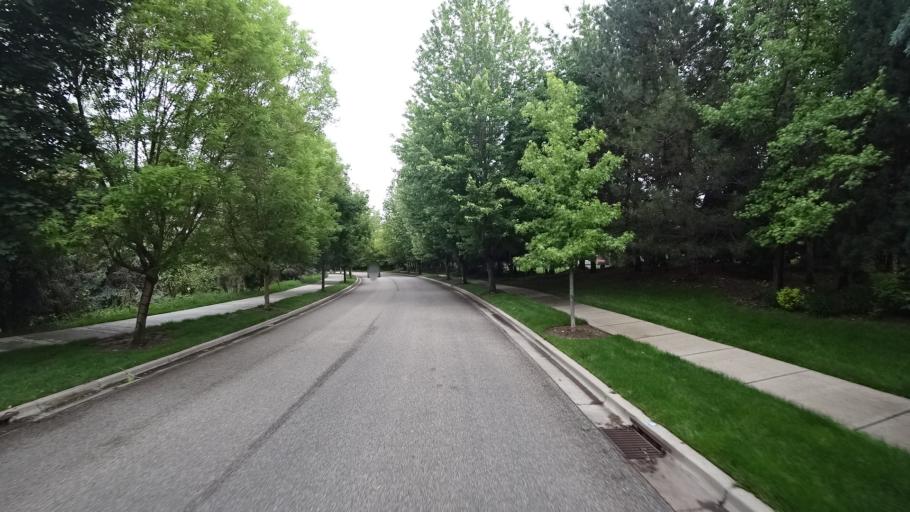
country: US
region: Idaho
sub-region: Ada County
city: Eagle
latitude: 43.6792
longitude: -116.3566
